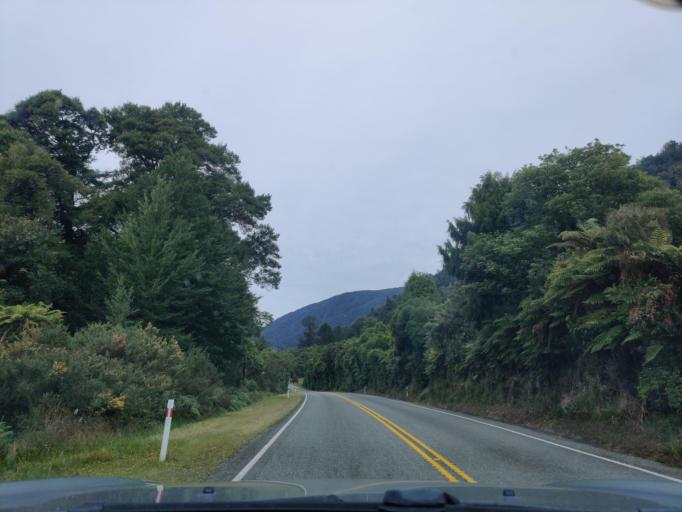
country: NZ
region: West Coast
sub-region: Buller District
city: Westport
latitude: -41.8310
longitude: 171.6507
